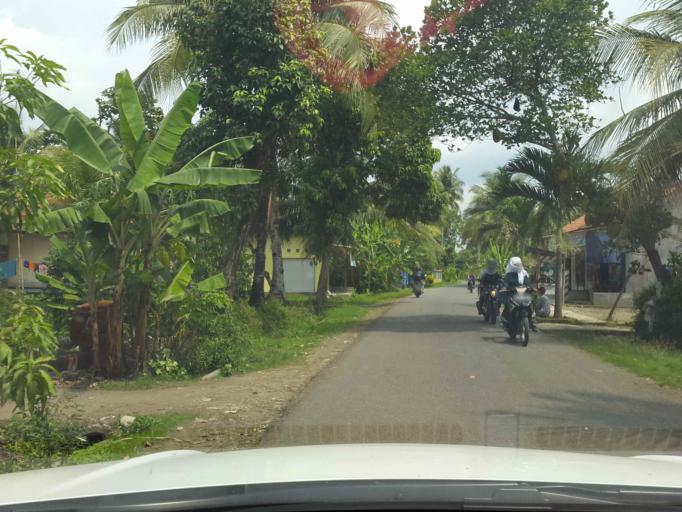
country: ID
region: Central Java
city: Gayamsari
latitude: -7.4369
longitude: 108.7360
